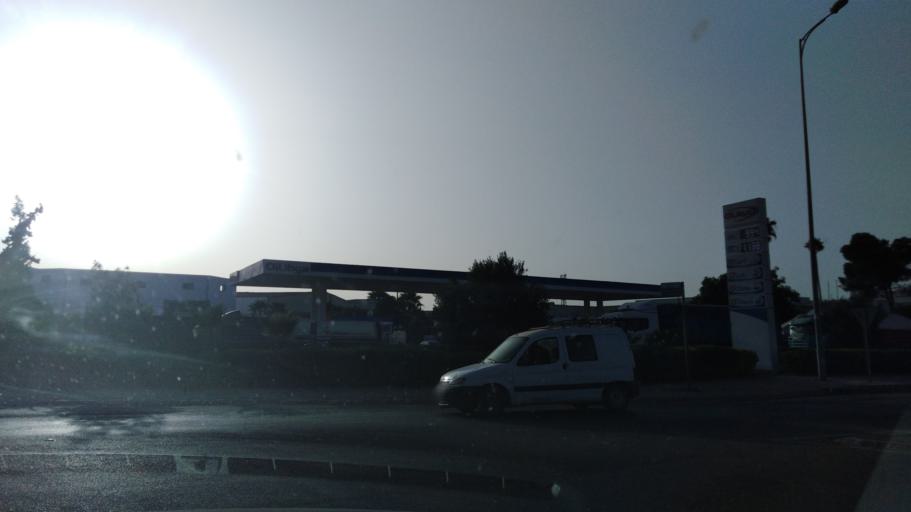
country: MA
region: Chaouia-Ouardigha
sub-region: Settat Province
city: Berrechid
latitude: 33.2442
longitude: -7.5865
